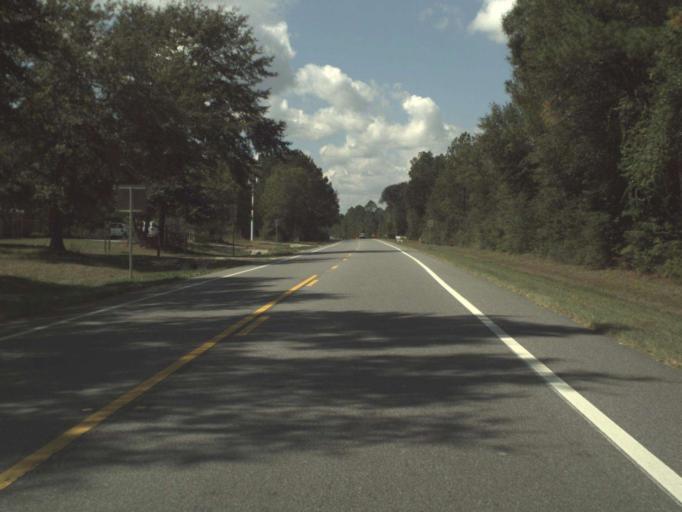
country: US
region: Florida
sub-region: Walton County
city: Freeport
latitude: 30.4725
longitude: -85.9674
